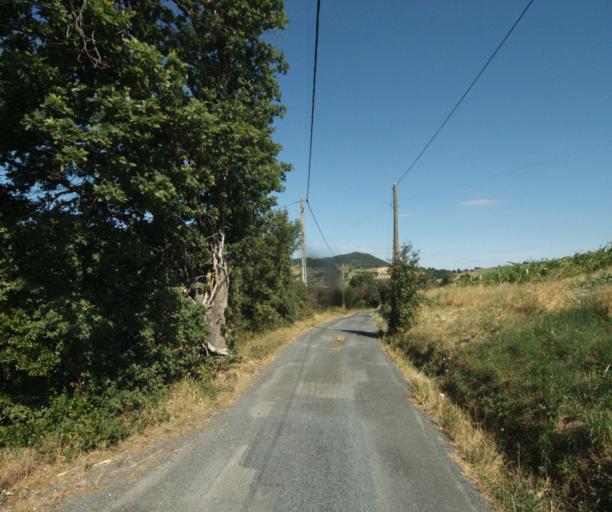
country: FR
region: Rhone-Alpes
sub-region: Departement du Rhone
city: Savigny
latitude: 45.8200
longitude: 4.5488
